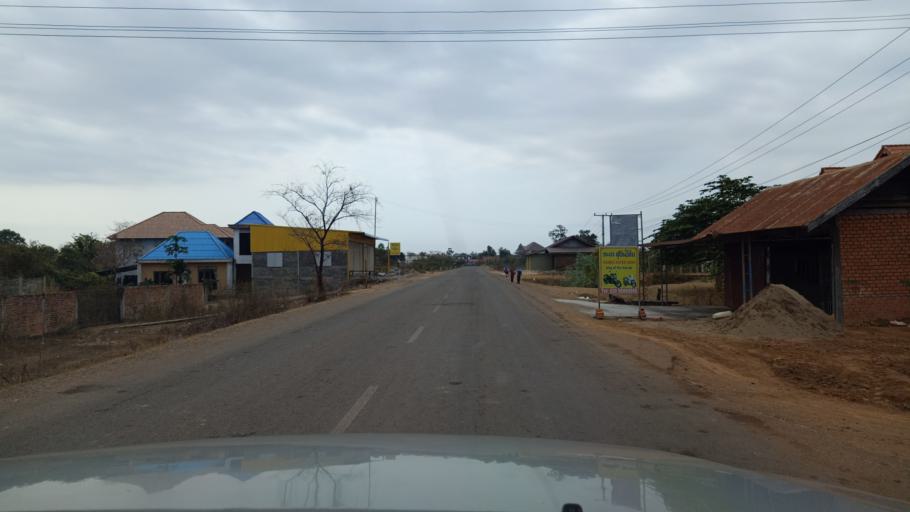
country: LA
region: Attapu
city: Attapu
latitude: 14.8028
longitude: 106.8492
